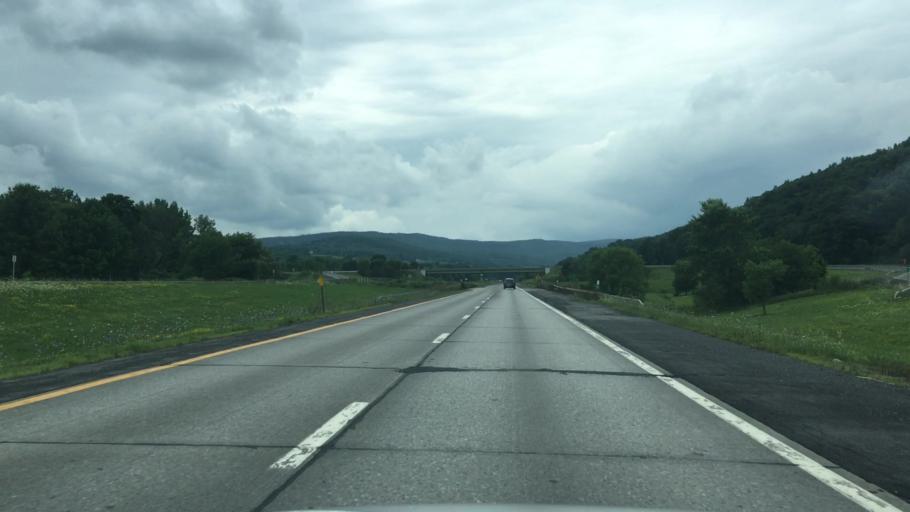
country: US
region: New York
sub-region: Schoharie County
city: Cobleskill
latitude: 42.6431
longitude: -74.5414
